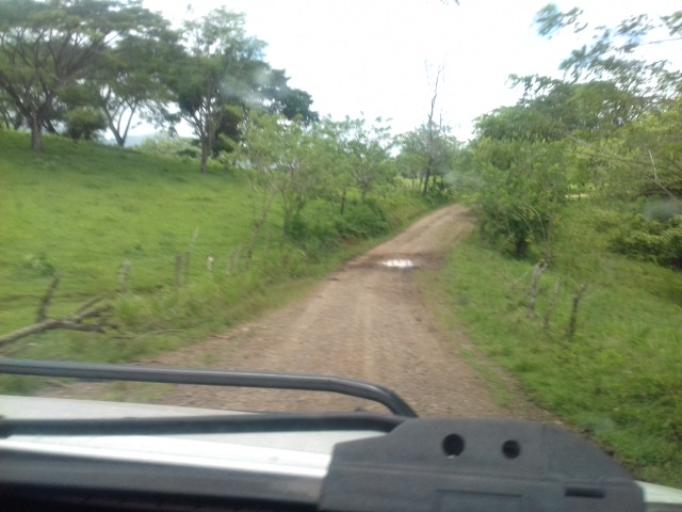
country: NI
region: Matagalpa
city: Matiguas
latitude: 13.0215
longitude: -85.4130
